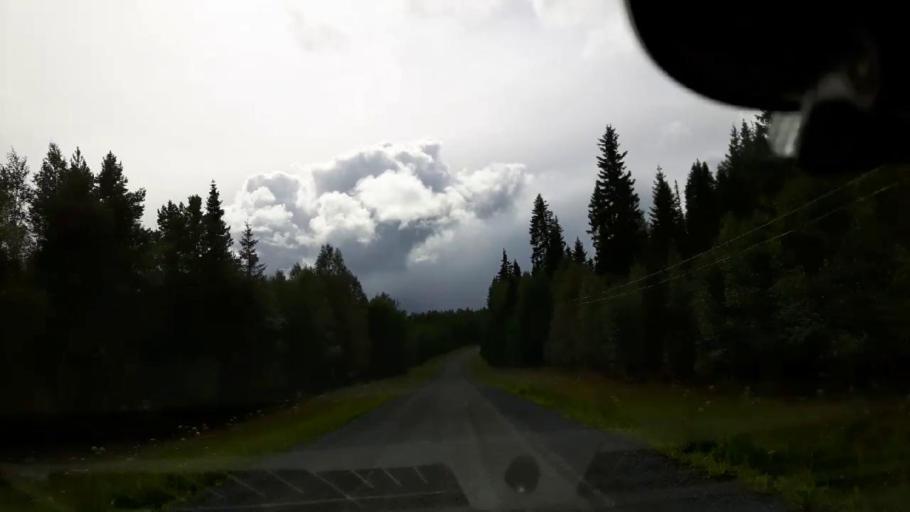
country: SE
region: Jaemtland
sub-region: Krokoms Kommun
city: Valla
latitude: 63.3583
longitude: 13.8550
